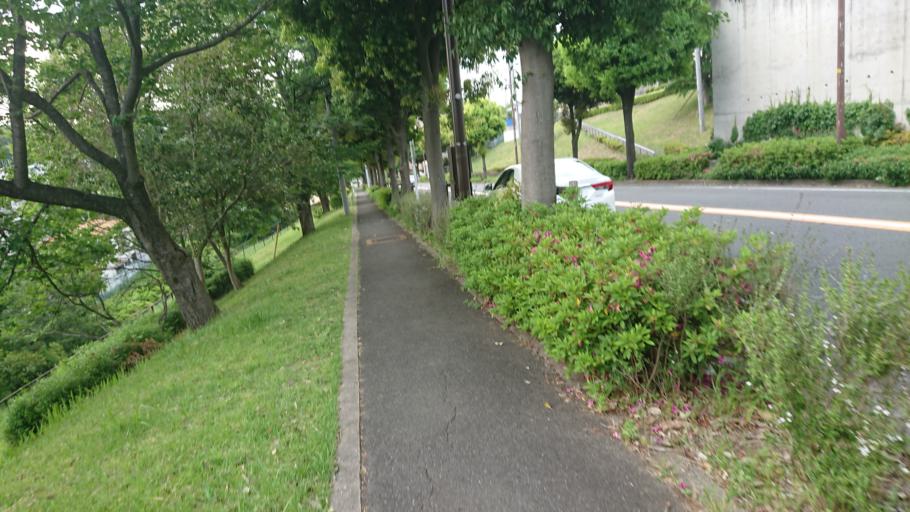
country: JP
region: Tokyo
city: Hino
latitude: 35.6392
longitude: 139.4527
